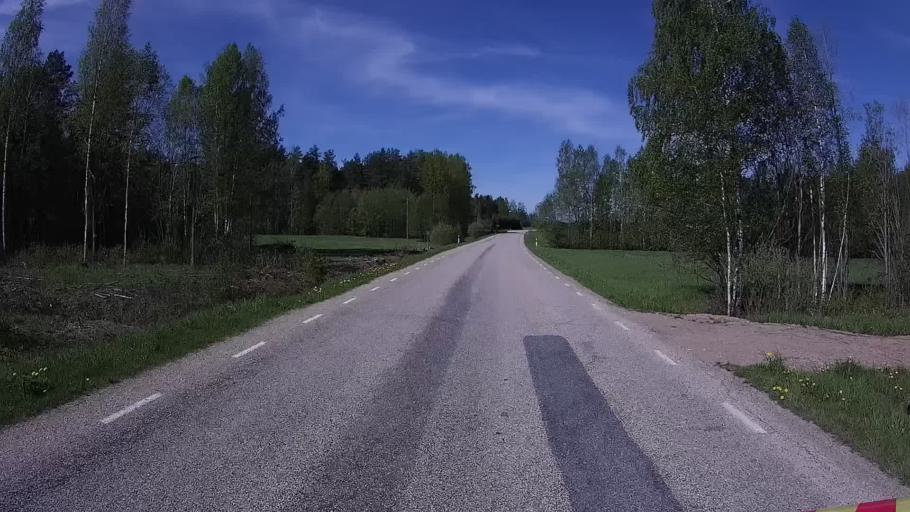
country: EE
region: Polvamaa
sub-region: Raepina vald
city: Rapina
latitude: 57.9669
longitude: 27.5427
